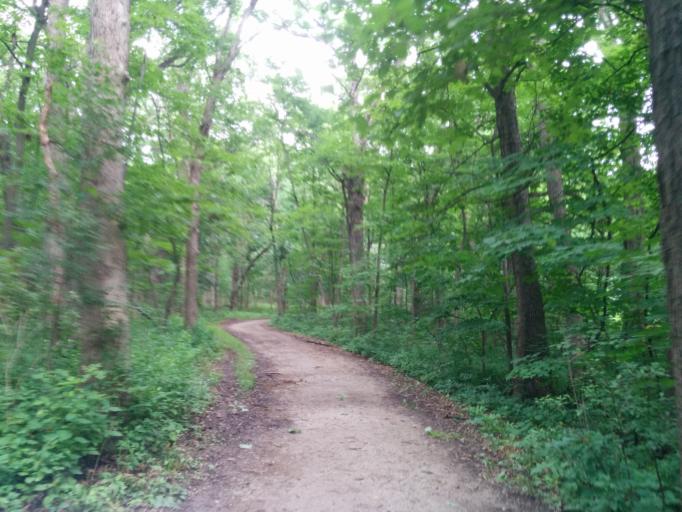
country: US
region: Illinois
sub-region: Cook County
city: Palos Park
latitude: 41.6762
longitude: -87.8419
